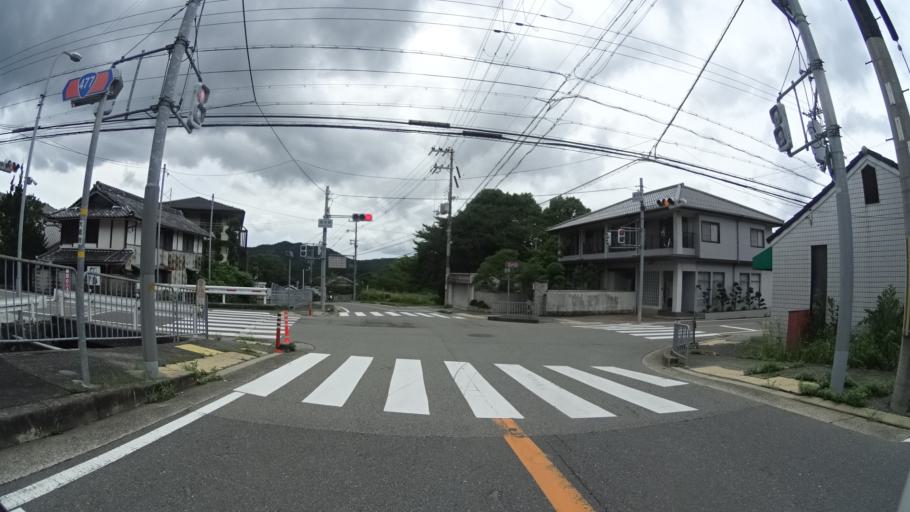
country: JP
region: Kyoto
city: Kameoka
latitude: 34.9708
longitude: 135.4655
